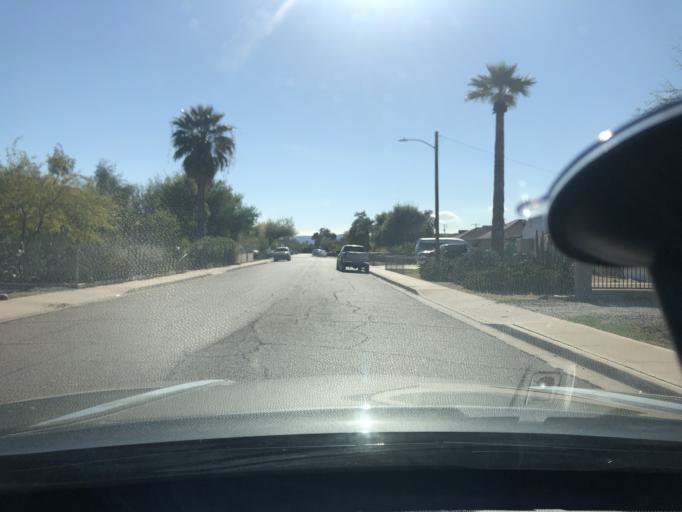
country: US
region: Arizona
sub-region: Maricopa County
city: Phoenix
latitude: 33.4715
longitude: -112.0290
